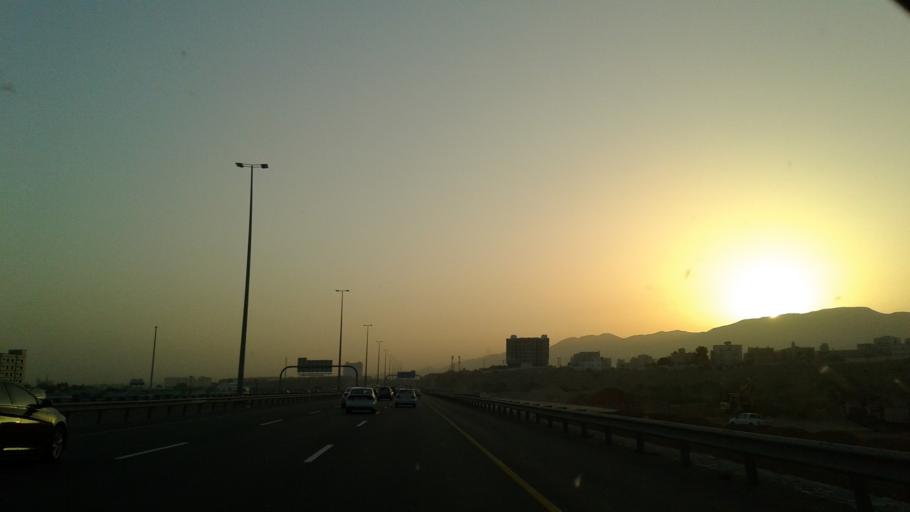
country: OM
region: Muhafazat Masqat
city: Bawshar
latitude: 23.5643
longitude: 58.3556
